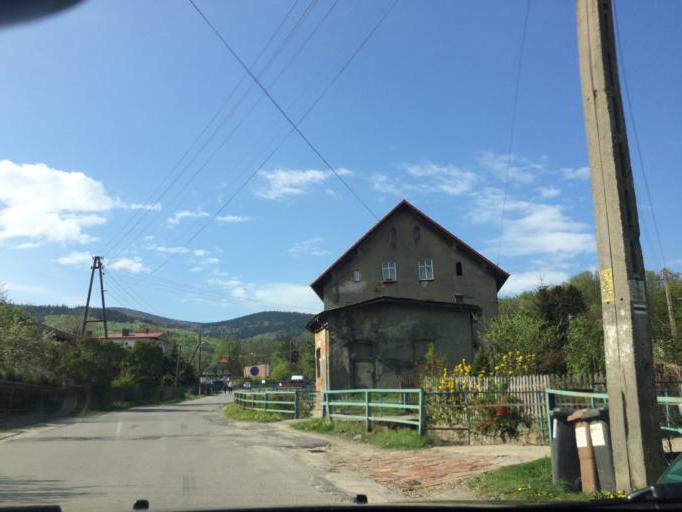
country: PL
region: Lower Silesian Voivodeship
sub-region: Powiat dzierzoniowski
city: Pieszyce
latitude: 50.6749
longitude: 16.5442
